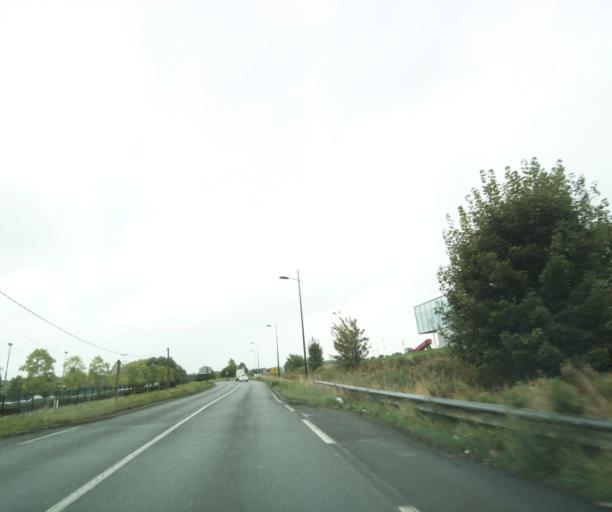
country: FR
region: Nord-Pas-de-Calais
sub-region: Departement du Nord
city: Roncq
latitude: 50.7645
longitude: 3.1241
